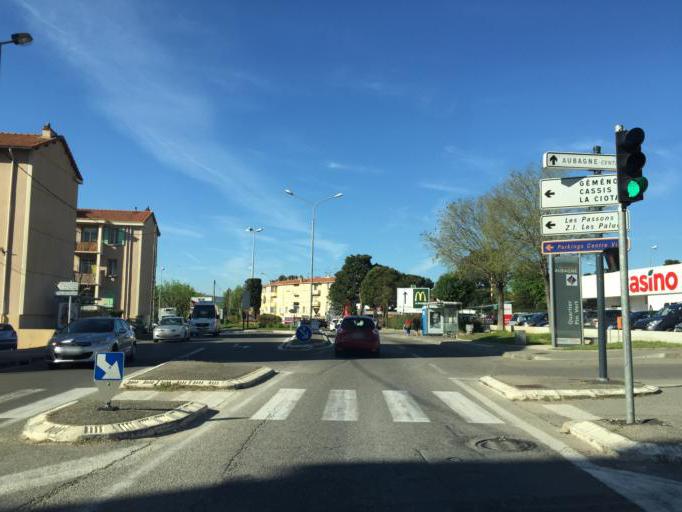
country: FR
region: Provence-Alpes-Cote d'Azur
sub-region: Departement des Bouches-du-Rhone
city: Aubagne
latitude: 43.3016
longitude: 5.5708
